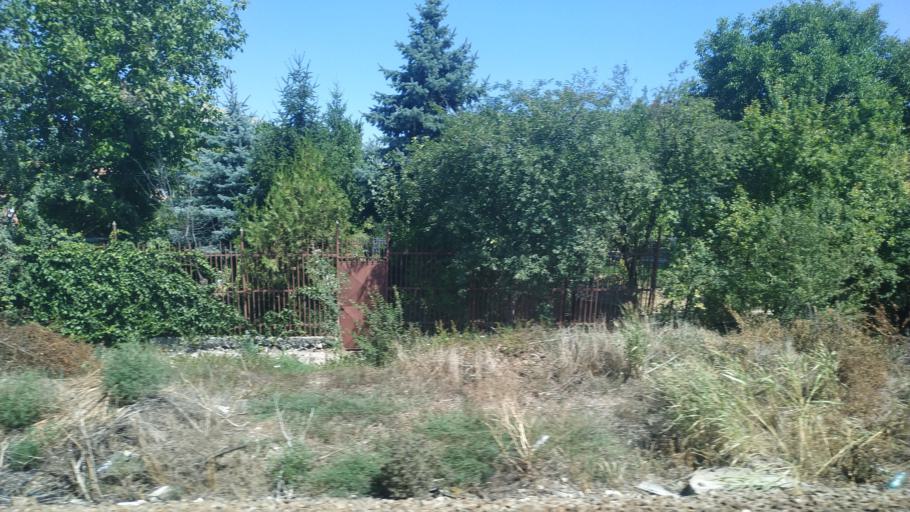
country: RO
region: Constanta
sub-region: Oras Murfatlar
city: Murfatlar
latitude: 44.1747
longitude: 28.4044
